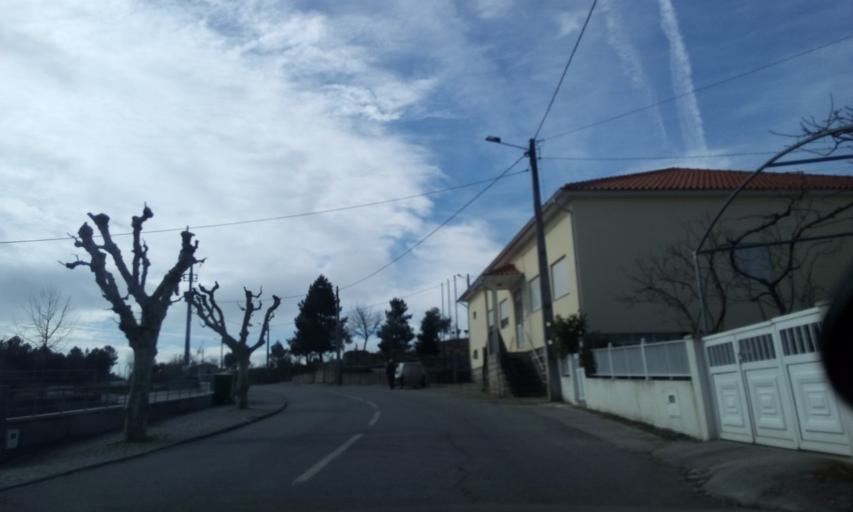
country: PT
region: Guarda
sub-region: Fornos de Algodres
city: Fornos de Algodres
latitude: 40.6786
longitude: -7.5303
